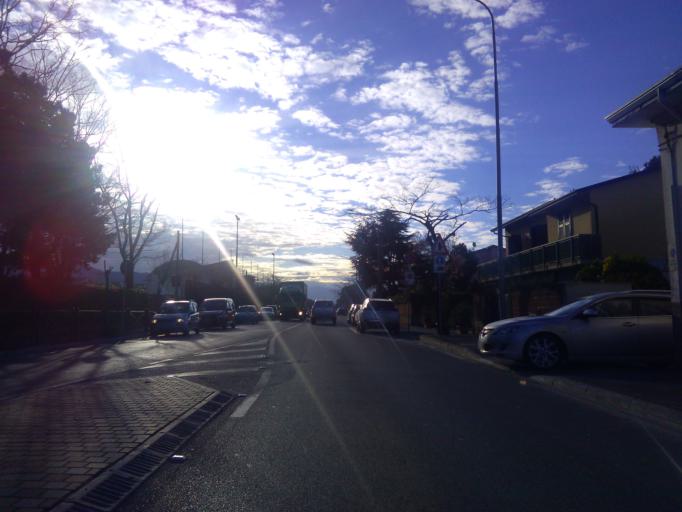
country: IT
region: Tuscany
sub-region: Provincia di Massa-Carrara
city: Marina di Carrara
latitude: 44.0523
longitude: 10.0447
